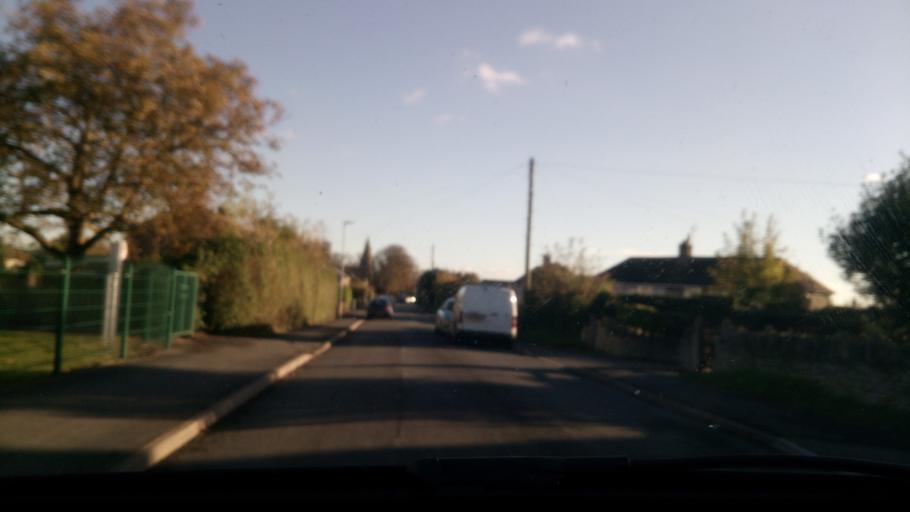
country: GB
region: England
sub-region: Peterborough
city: Wittering
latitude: 52.6079
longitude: -0.4439
